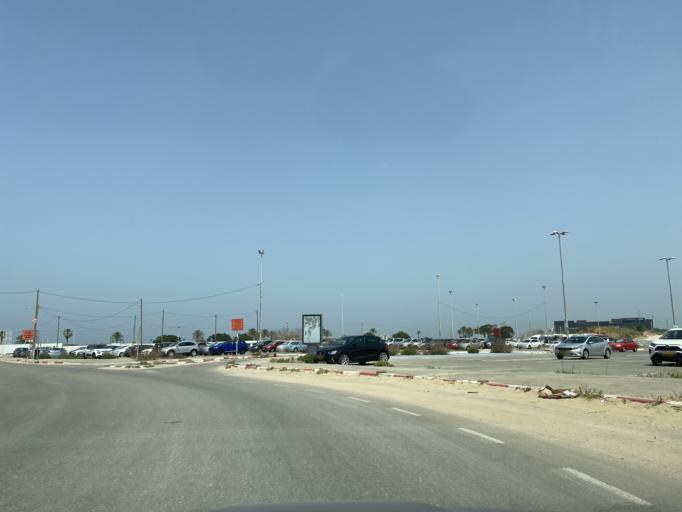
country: IL
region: Tel Aviv
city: Herzliyya
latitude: 32.1470
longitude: 34.8067
